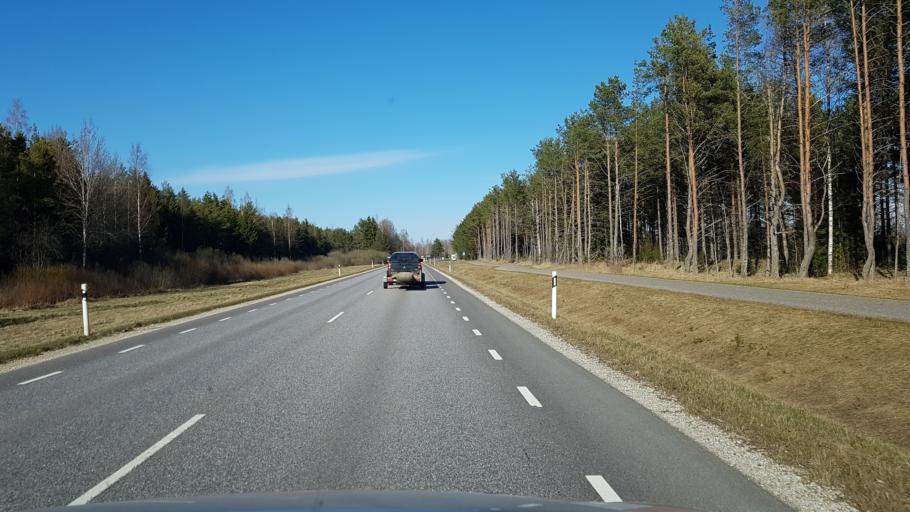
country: EE
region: Jogevamaa
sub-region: Mustvee linn
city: Mustvee
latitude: 58.9278
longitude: 27.0191
